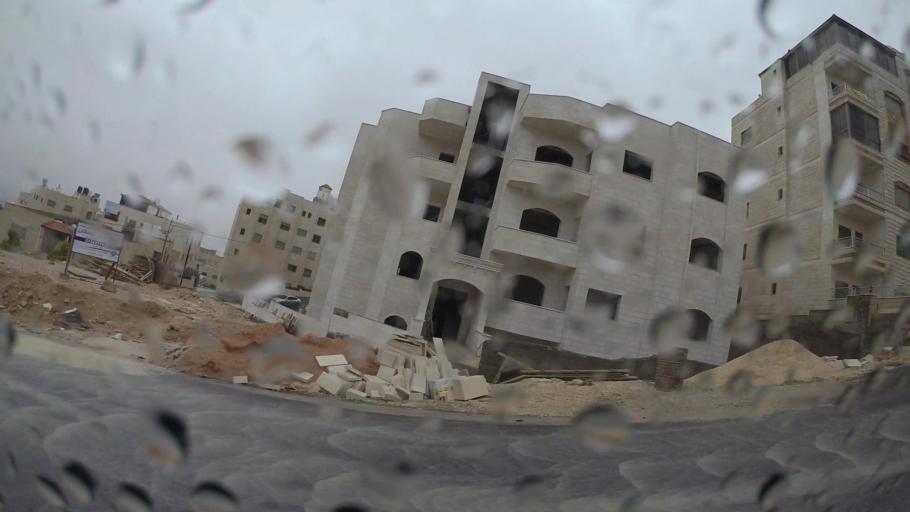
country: JO
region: Amman
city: Al Jubayhah
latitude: 32.0282
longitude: 35.8865
